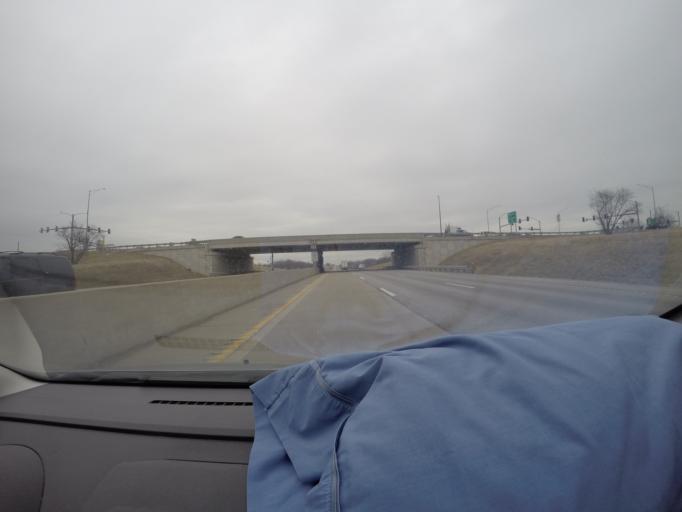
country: US
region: Missouri
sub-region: Saint Charles County
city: Lake Saint Louis
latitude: 38.8040
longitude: -90.7715
